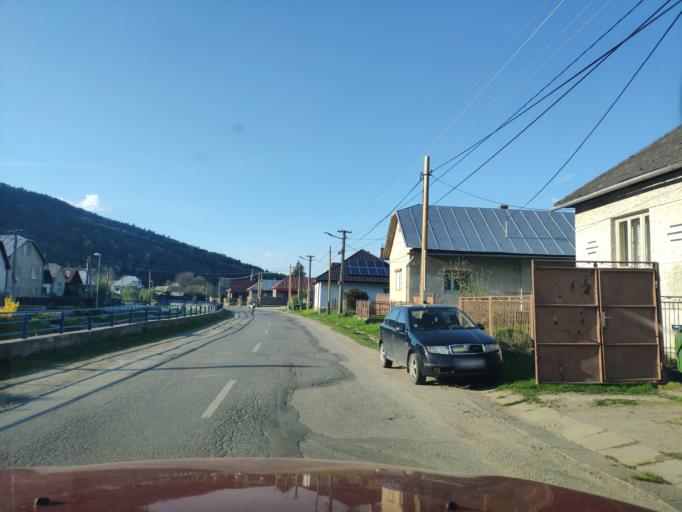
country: SK
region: Presovsky
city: Lipany
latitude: 49.0991
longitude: 20.8496
